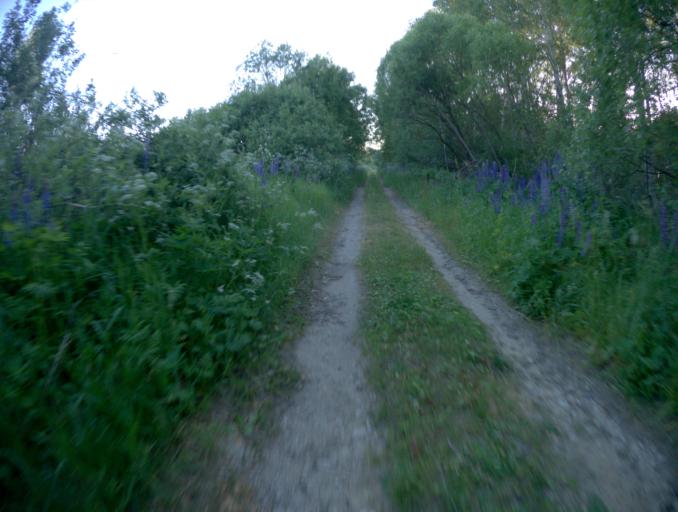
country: RU
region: Vladimir
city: Golovino
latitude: 55.9864
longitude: 40.5409
